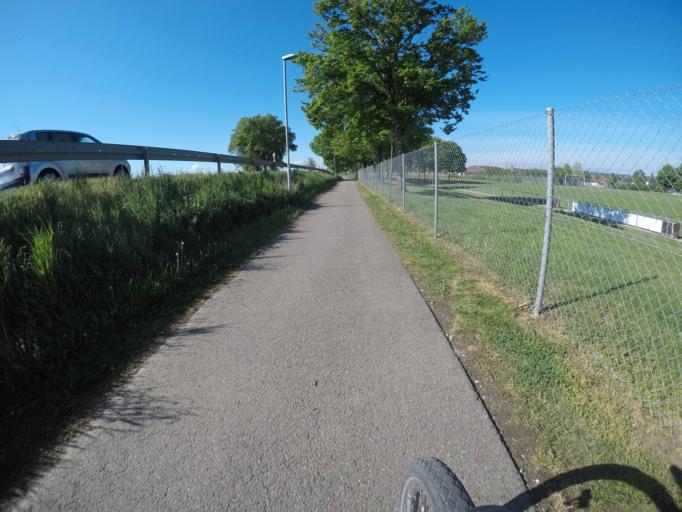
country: DE
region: Baden-Wuerttemberg
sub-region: Regierungsbezirk Stuttgart
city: Altenriet
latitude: 48.5909
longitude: 9.1926
